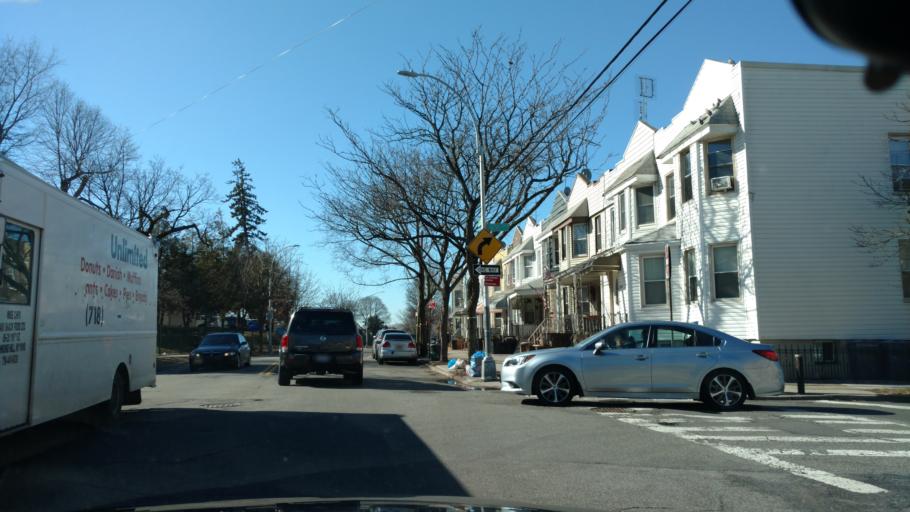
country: US
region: New York
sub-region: Kings County
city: East New York
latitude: 40.7010
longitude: -73.8823
